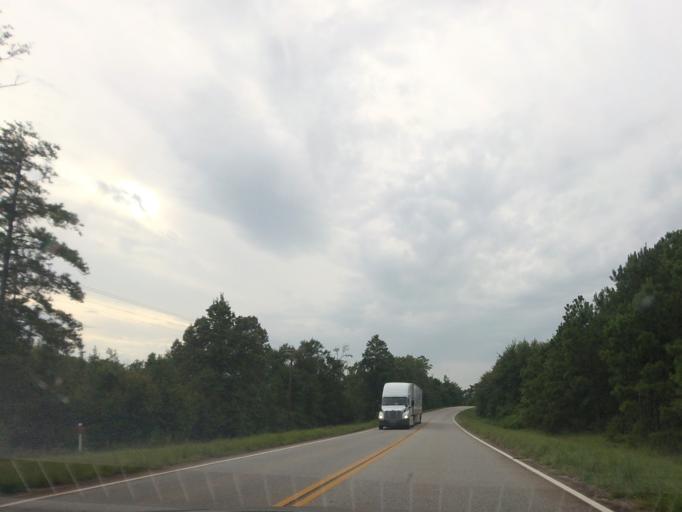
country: US
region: Georgia
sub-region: Twiggs County
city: Jeffersonville
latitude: 32.7216
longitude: -83.4141
